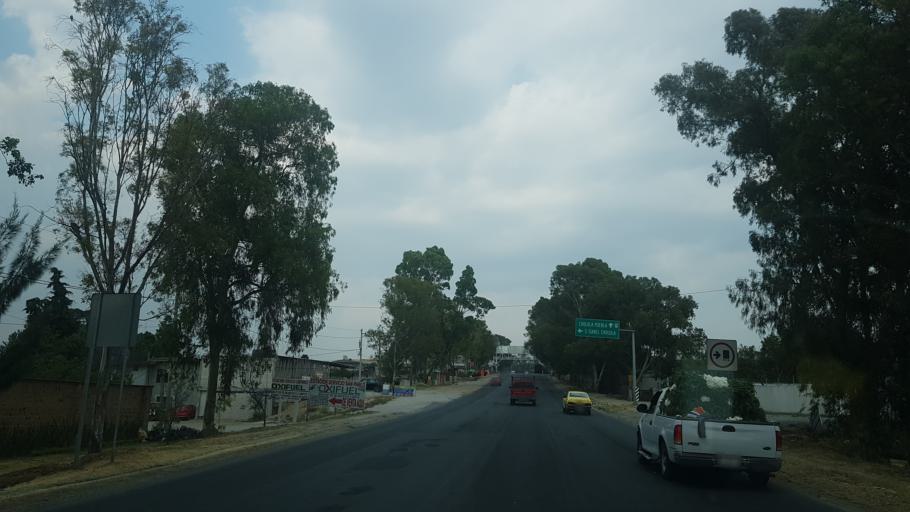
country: MX
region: Puebla
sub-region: Santa Isabel Cholula
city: San Pablo Ahuatempa
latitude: 18.9827
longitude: -98.3668
